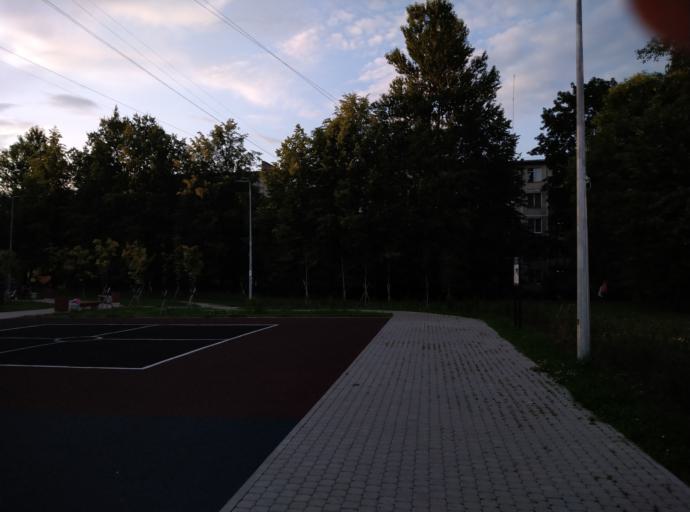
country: RU
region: St.-Petersburg
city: Kupchino
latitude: 59.8561
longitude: 30.3452
